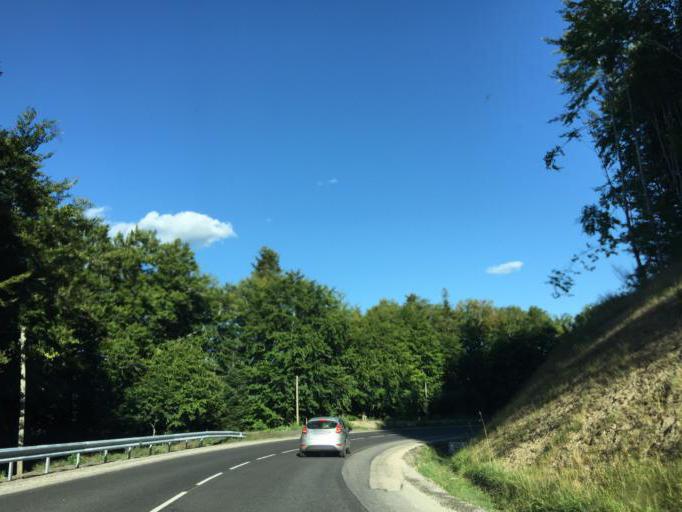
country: FR
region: Auvergne
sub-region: Departement de la Haute-Loire
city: Saugues
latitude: 44.9826
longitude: 3.6153
